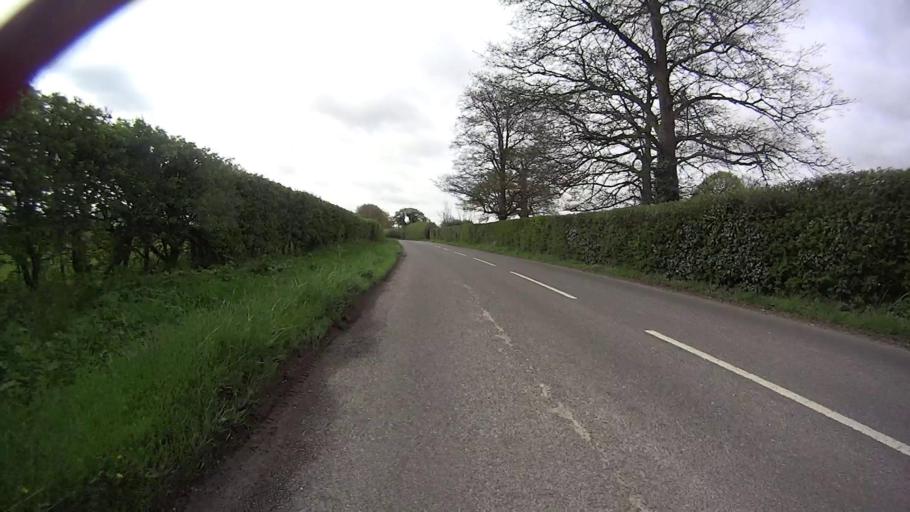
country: GB
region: England
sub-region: Surrey
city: Newdigate
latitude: 51.1156
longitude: -0.2893
